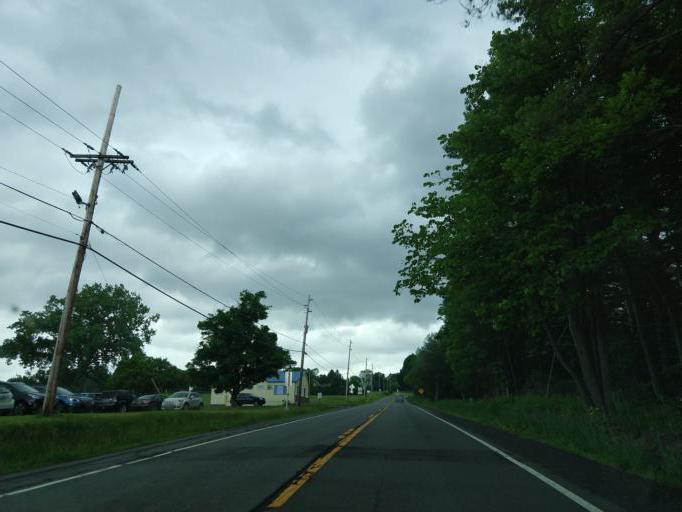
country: US
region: New York
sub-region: Tompkins County
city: Northwest Ithaca
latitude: 42.5430
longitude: -76.5308
